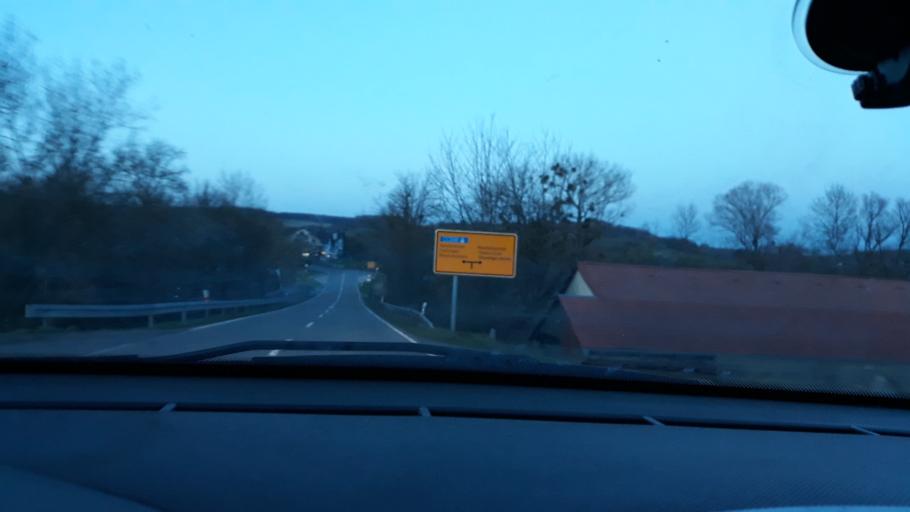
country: DE
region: Saarland
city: Kleinblittersdorf
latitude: 49.1569
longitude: 7.0874
